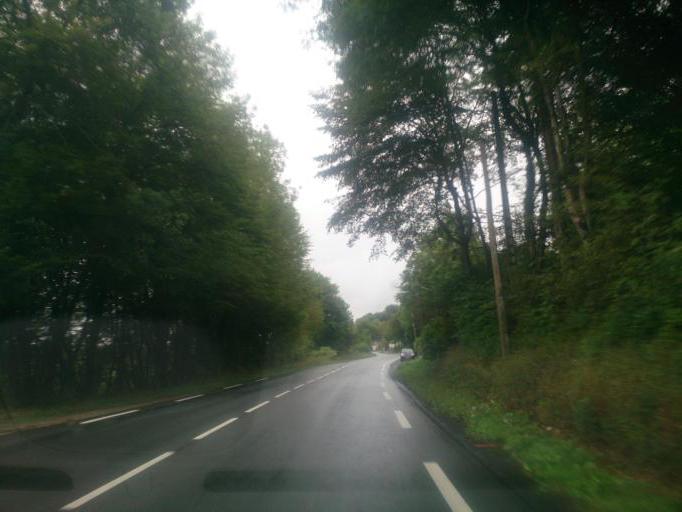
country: FR
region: Limousin
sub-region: Departement de la Correze
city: Malemort-sur-Correze
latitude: 45.1763
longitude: 1.5666
